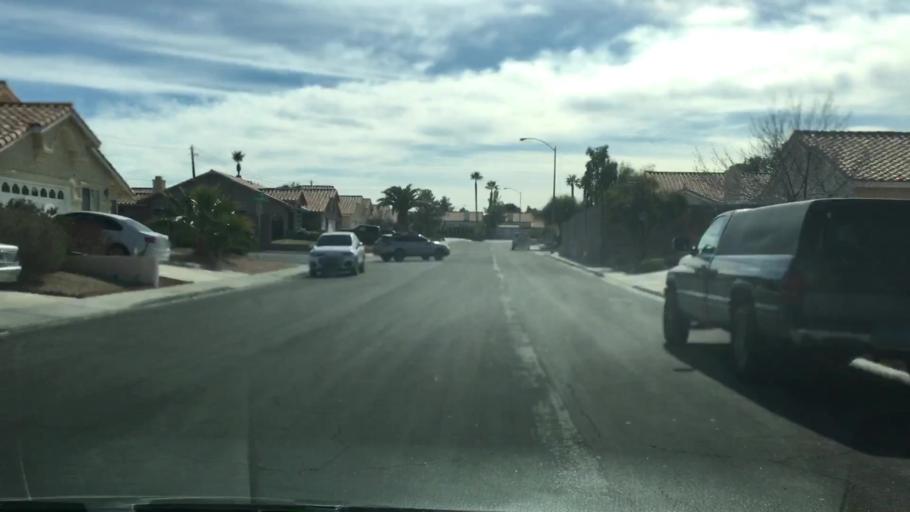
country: US
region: Nevada
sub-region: Clark County
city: Whitney
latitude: 36.0480
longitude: -115.1279
